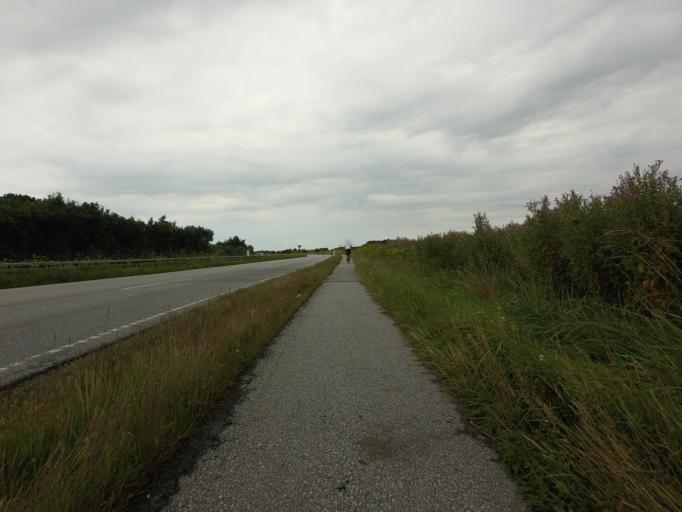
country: DK
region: North Denmark
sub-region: Alborg Kommune
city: Vadum
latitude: 57.1033
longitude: 9.8835
